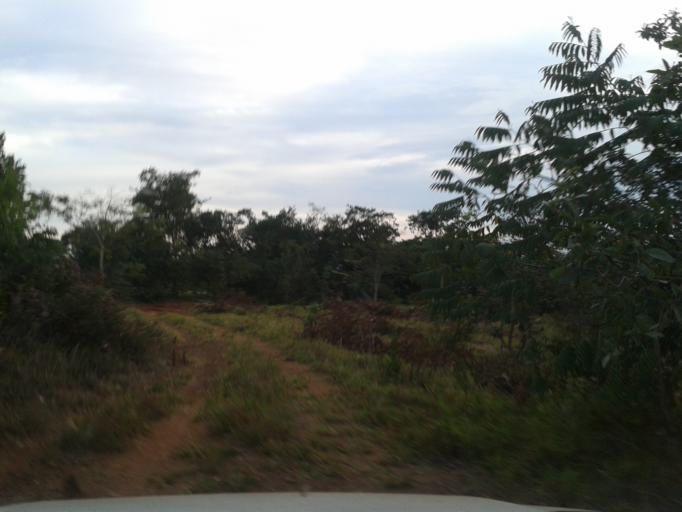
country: BR
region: Minas Gerais
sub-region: Campina Verde
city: Campina Verde
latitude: -19.4138
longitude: -49.6164
